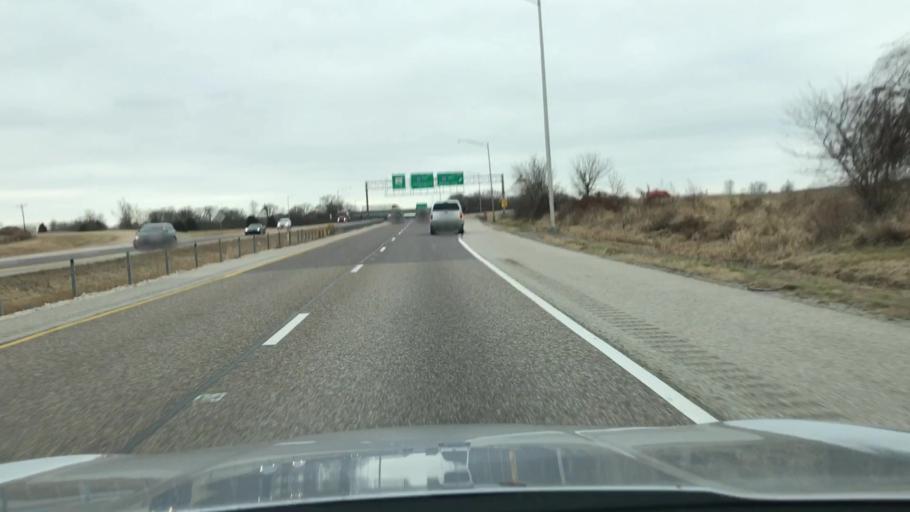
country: US
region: Illinois
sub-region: Madison County
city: Troy
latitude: 38.7567
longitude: -89.9061
